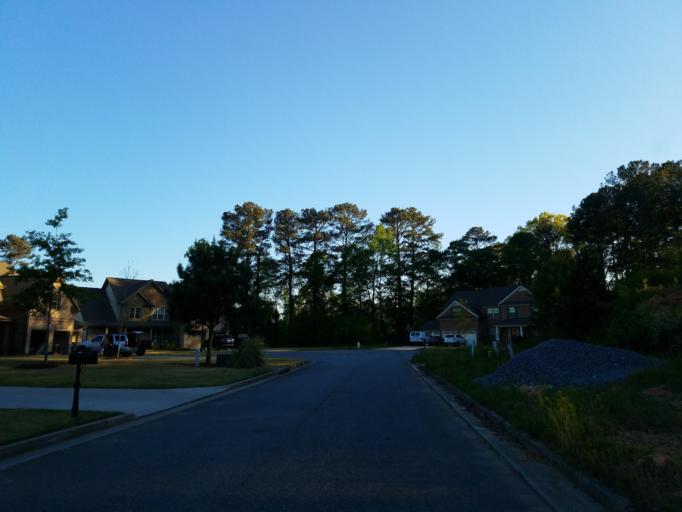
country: US
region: Georgia
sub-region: Cobb County
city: Powder Springs
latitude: 33.9179
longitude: -84.6356
